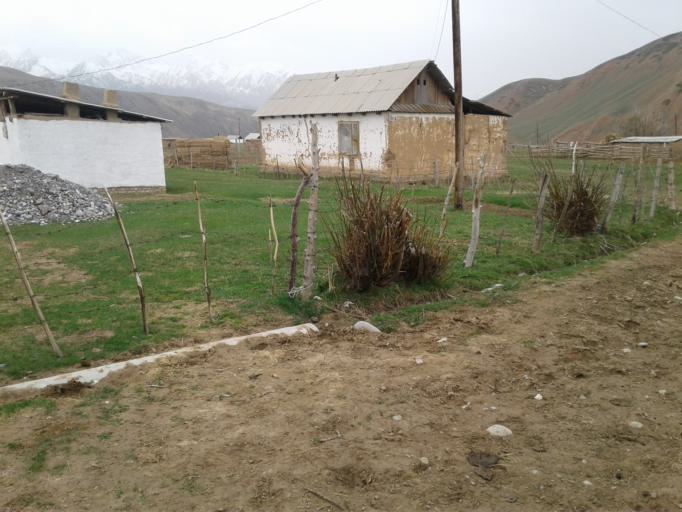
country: KG
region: Naryn
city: Naryn
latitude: 41.5148
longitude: 76.4362
